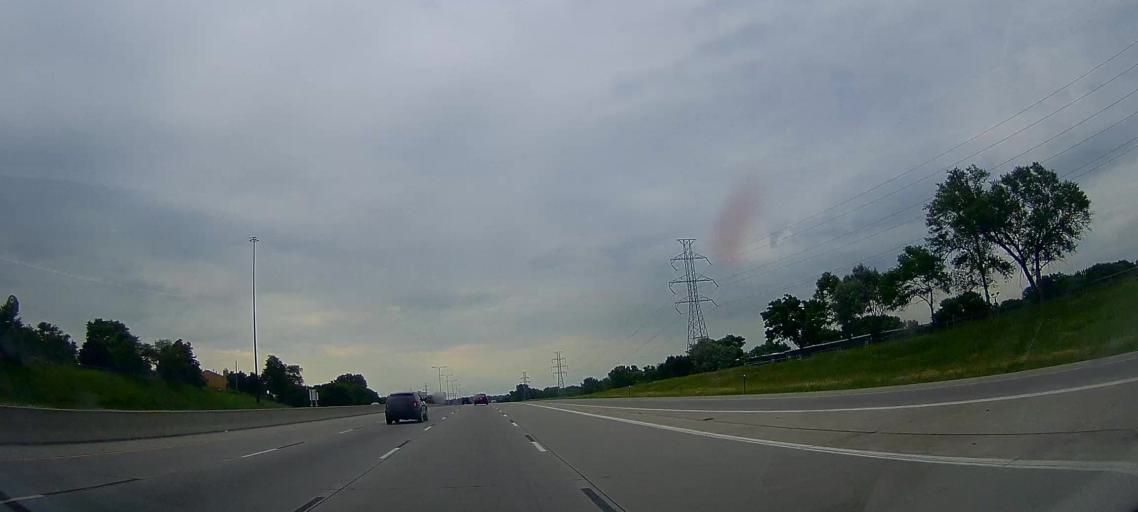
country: US
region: Nebraska
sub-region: Douglas County
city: Ralston
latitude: 41.2883
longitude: -96.0748
